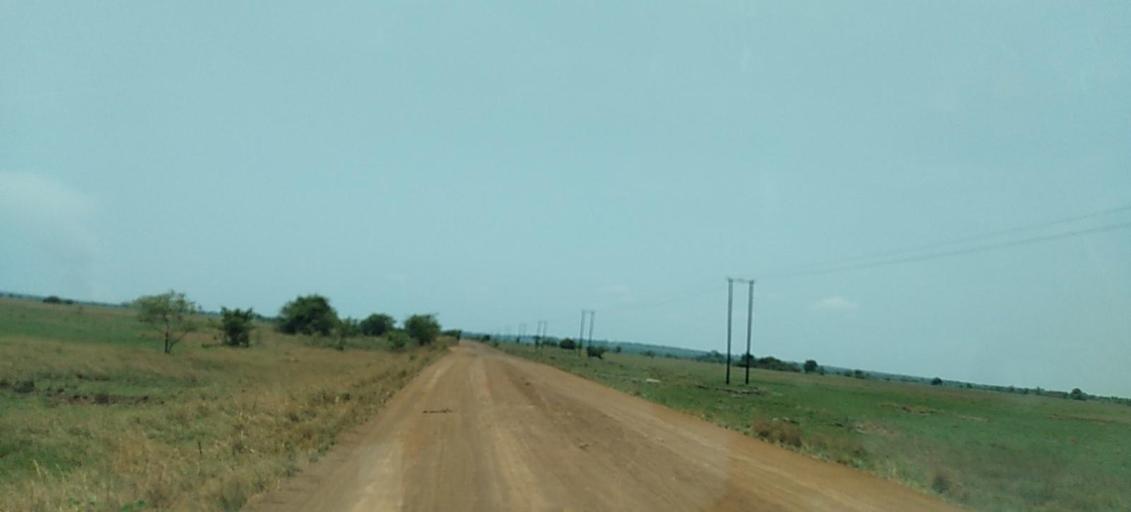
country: ZM
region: Copperbelt
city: Mpongwe
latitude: -13.6606
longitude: 27.8507
